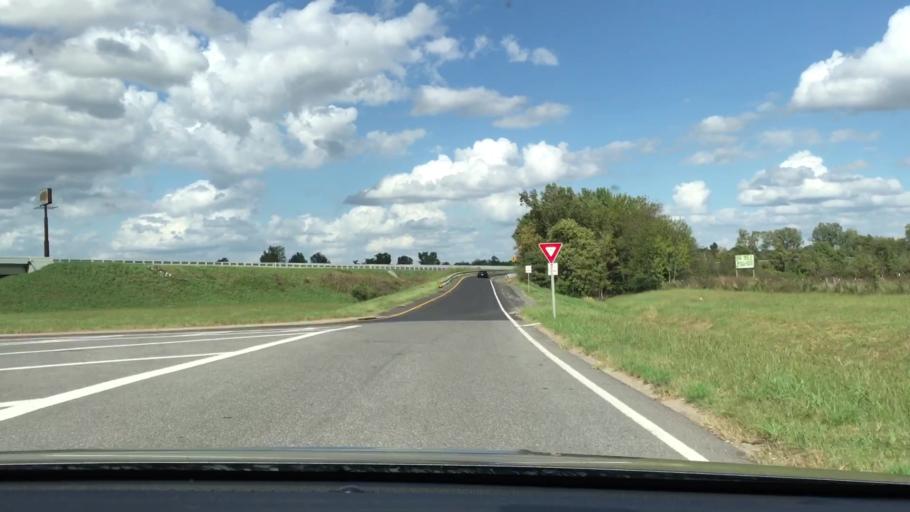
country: US
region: Kentucky
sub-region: Graves County
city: Mayfield
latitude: 36.7662
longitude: -88.6426
